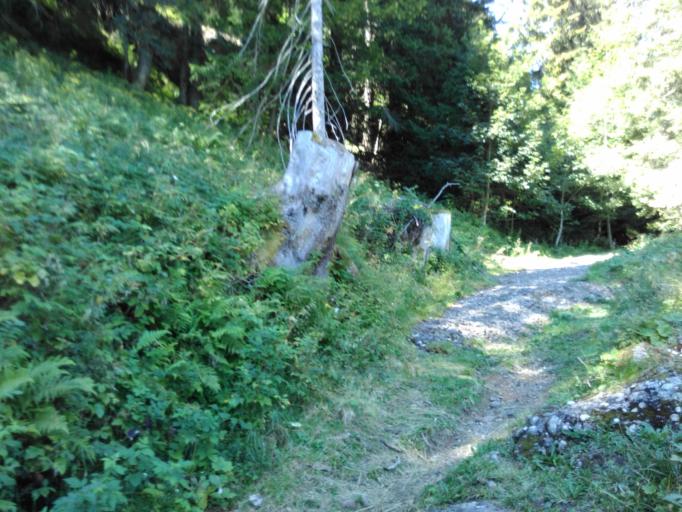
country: CH
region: Lucerne
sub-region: Lucerne-Land District
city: Vitznau
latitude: 47.0472
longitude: 8.4781
